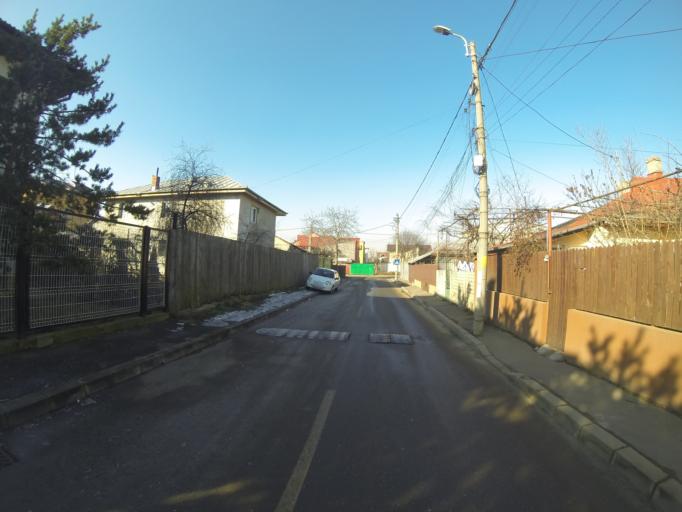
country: RO
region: Ilfov
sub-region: Comuna Magurele
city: Magurele
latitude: 44.3925
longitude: 26.0580
